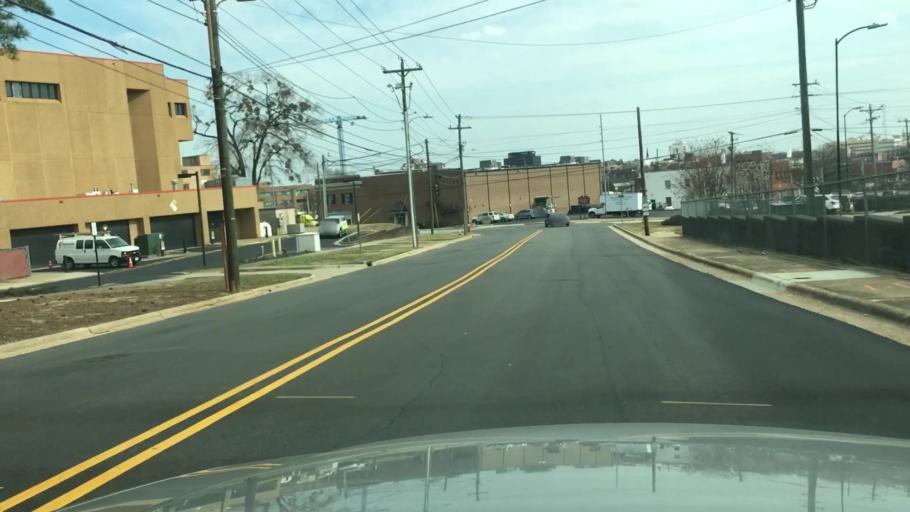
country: US
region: North Carolina
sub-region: Cumberland County
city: Fayetteville
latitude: 35.0531
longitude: -78.8903
